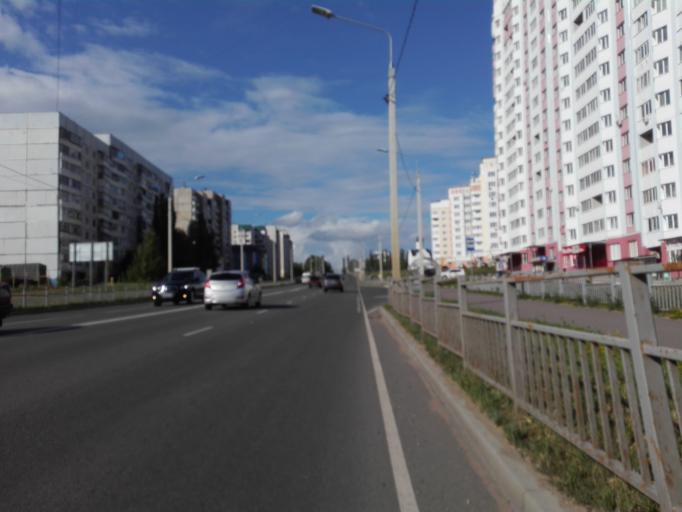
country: RU
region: Orjol
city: Orel
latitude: 53.0135
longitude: 36.1311
